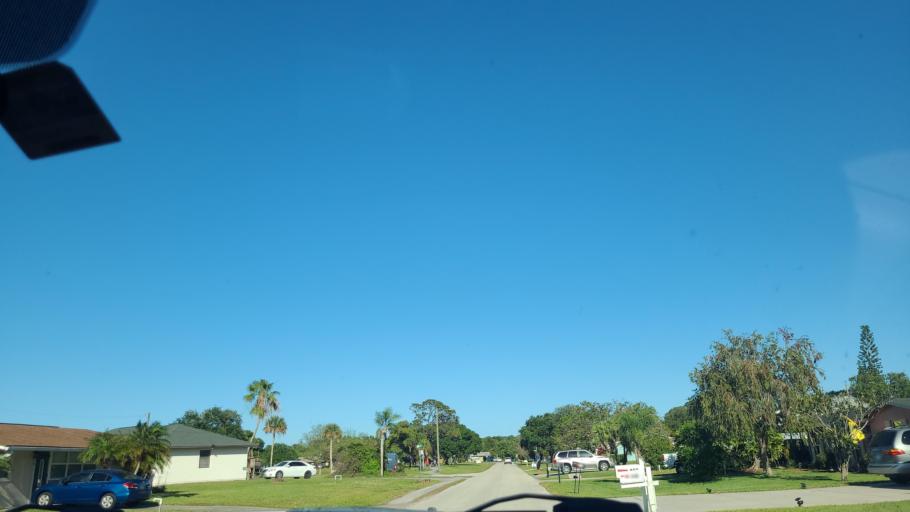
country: US
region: Florida
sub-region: Indian River County
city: Sebastian
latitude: 27.7999
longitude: -80.4836
